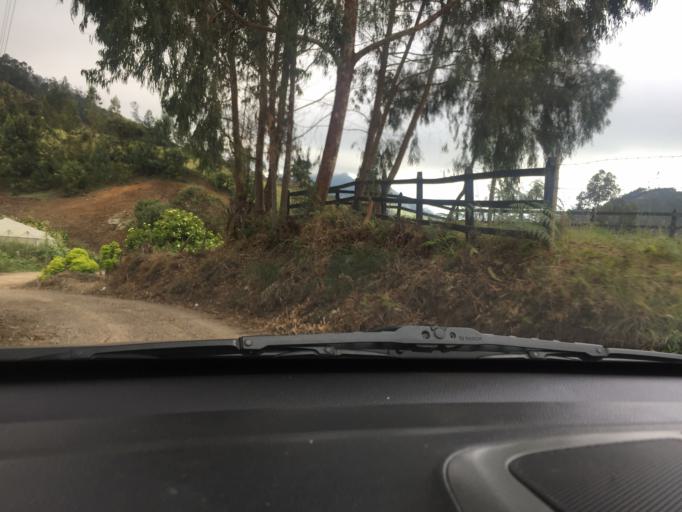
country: CO
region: Cundinamarca
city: Zipacon
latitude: 4.7515
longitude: -74.3711
